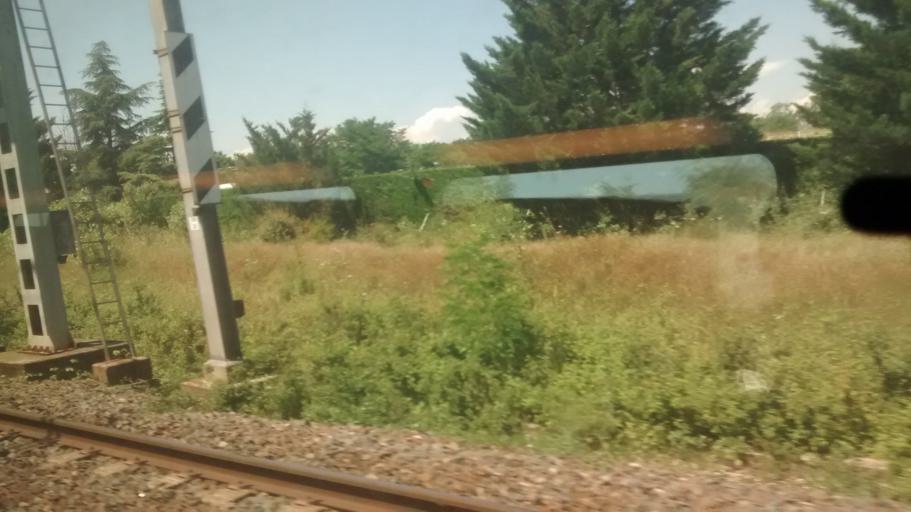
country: FR
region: Rhone-Alpes
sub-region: Departement du Rhone
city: Sathonay-Village
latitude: 45.8236
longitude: 4.8834
